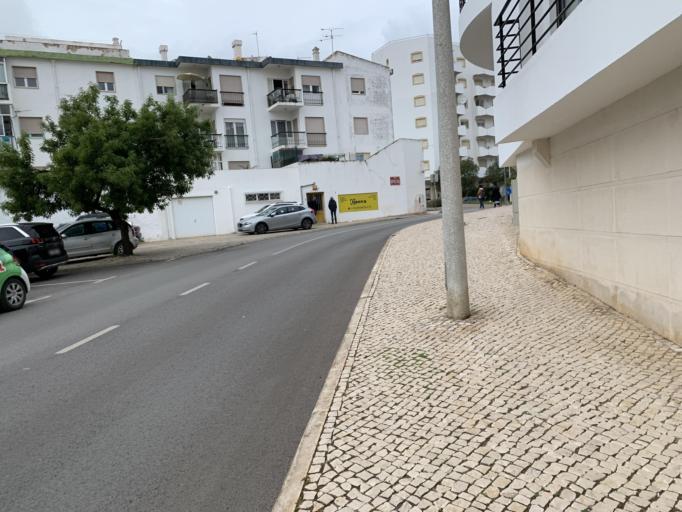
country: PT
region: Faro
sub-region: Lagos
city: Lagos
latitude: 37.1004
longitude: -8.6775
